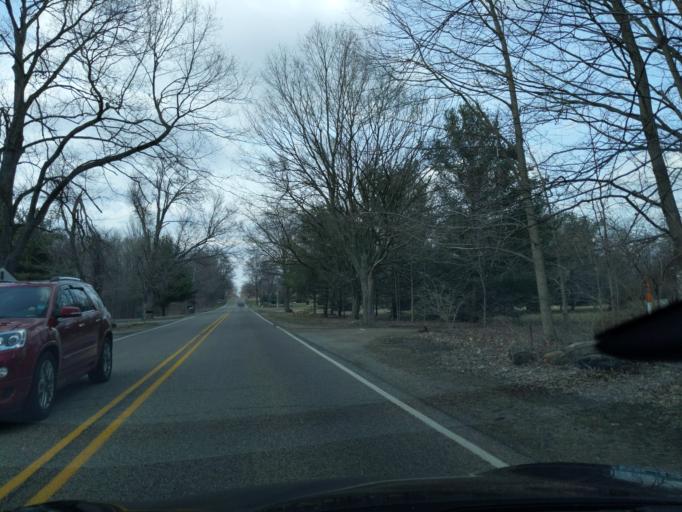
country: US
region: Michigan
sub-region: Jackson County
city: Jackson
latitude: 42.3115
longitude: -84.4136
